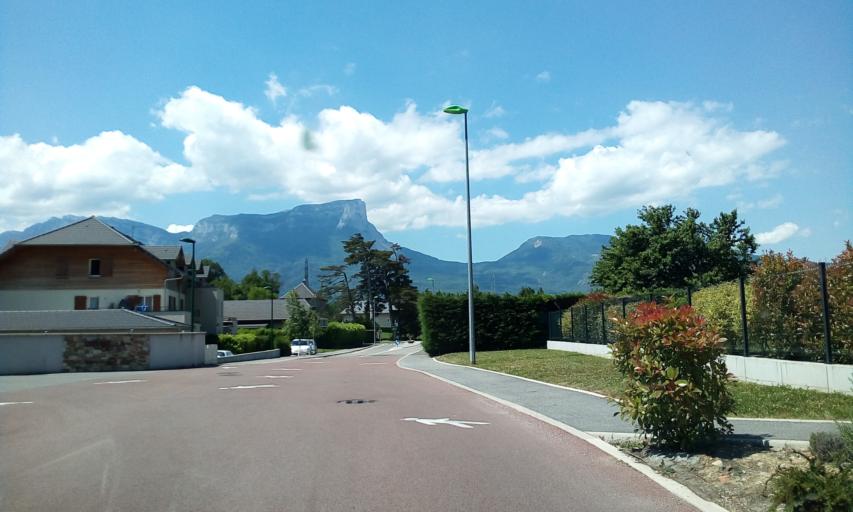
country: FR
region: Rhone-Alpes
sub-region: Departement de la Savoie
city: Les Marches
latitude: 45.5003
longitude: 6.0246
